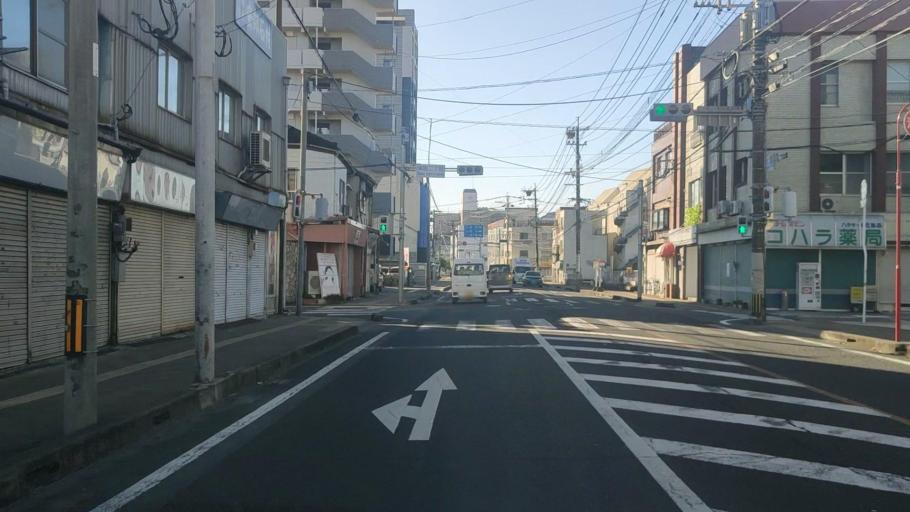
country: JP
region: Miyazaki
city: Nobeoka
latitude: 32.5882
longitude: 131.6711
